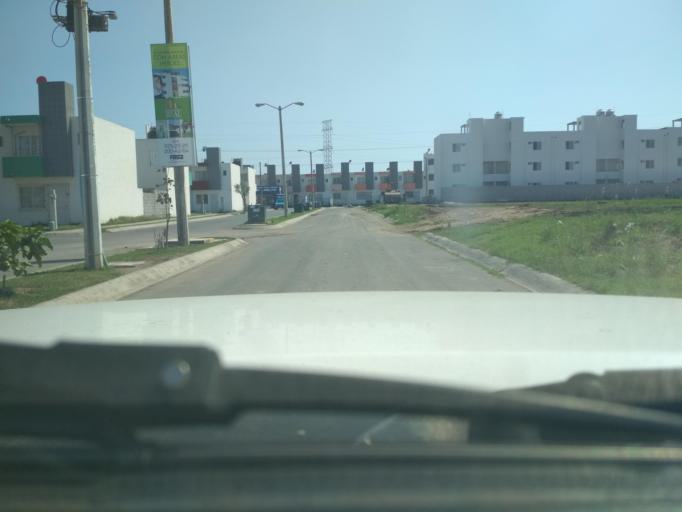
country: MX
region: Veracruz
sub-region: Veracruz
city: Las Amapolas
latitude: 19.1574
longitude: -96.2229
